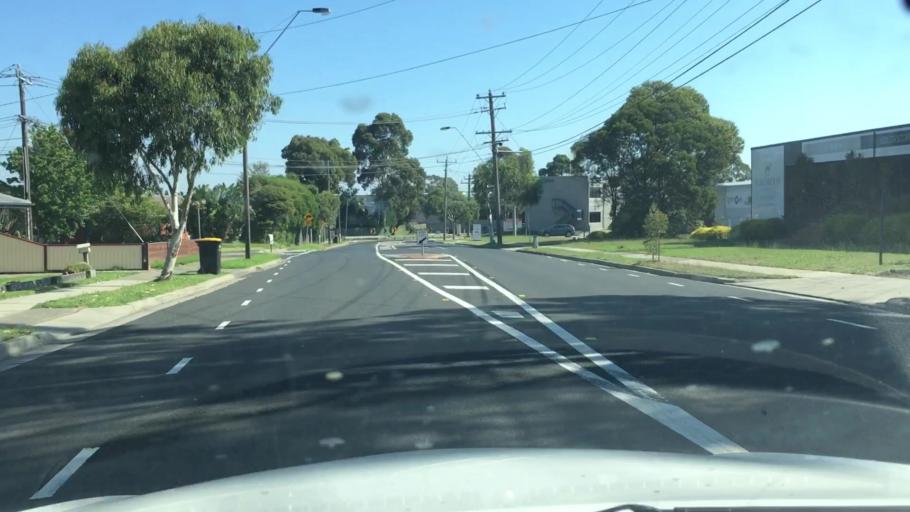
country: AU
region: Victoria
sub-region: Greater Dandenong
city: Noble Park North
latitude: -37.9483
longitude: 145.1874
